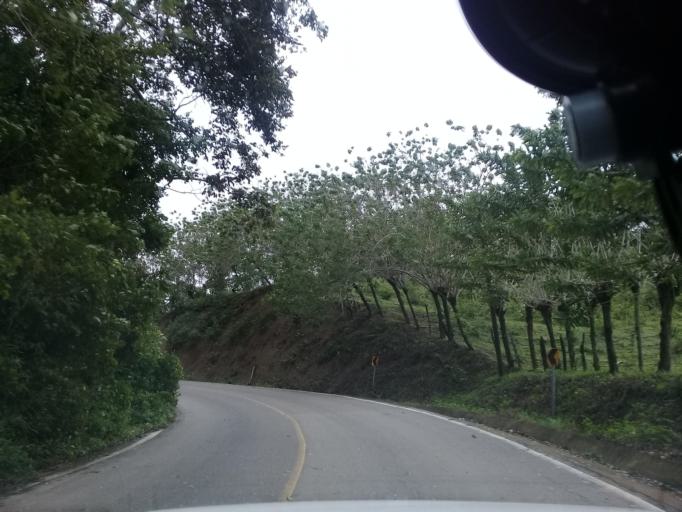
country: MX
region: Veracruz
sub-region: Chalma
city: San Pedro Coyutla
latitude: 21.2133
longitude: -98.4259
